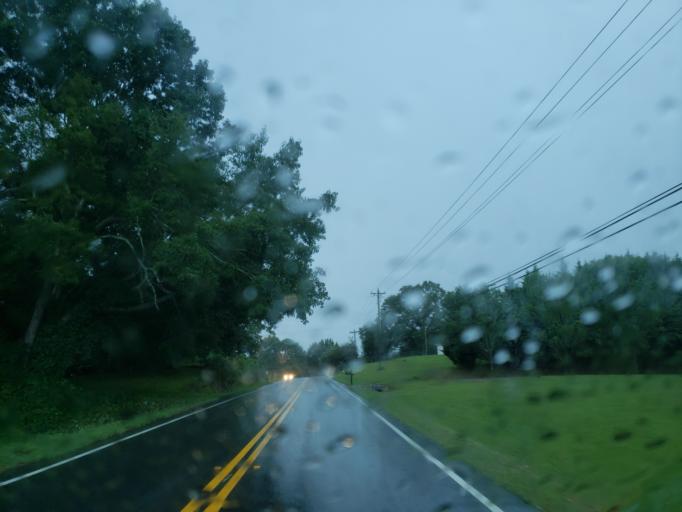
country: US
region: Georgia
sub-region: Cherokee County
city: Canton
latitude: 34.3075
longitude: -84.4606
